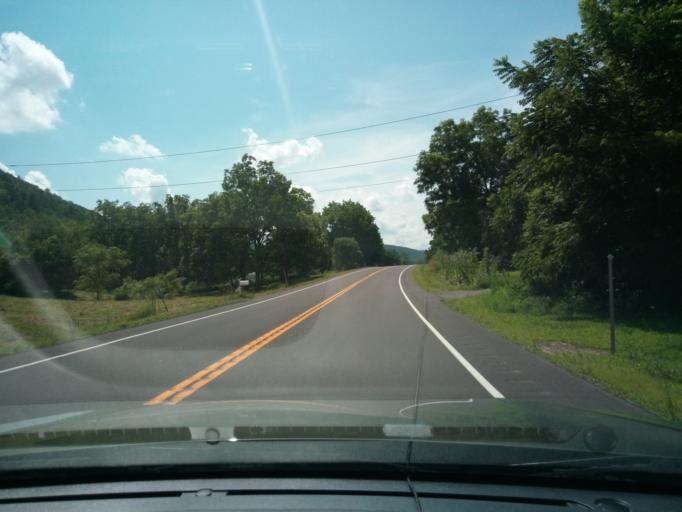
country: US
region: New York
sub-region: Chemung County
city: Southport
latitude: 42.0199
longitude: -76.6810
